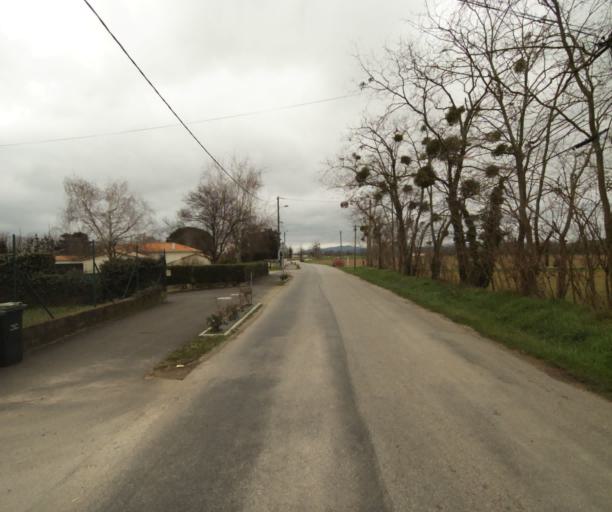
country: FR
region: Midi-Pyrenees
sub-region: Departement de l'Ariege
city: Pamiers
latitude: 43.1488
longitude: 1.6350
